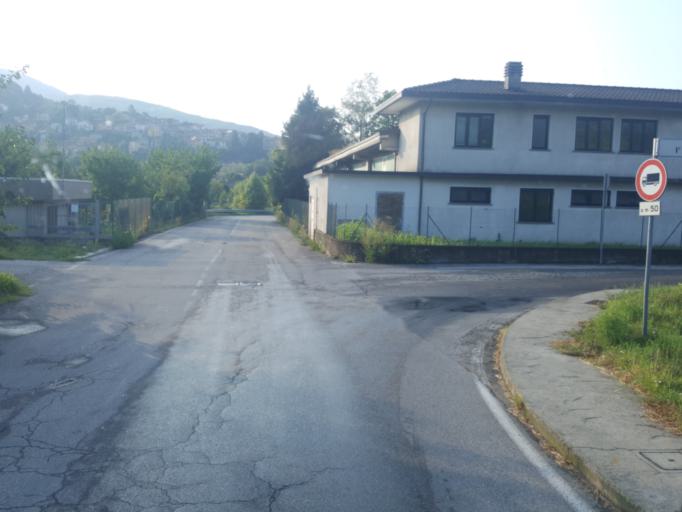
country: IT
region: Lombardy
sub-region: Provincia di Varese
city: Gemonio
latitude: 45.8834
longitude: 8.6661
